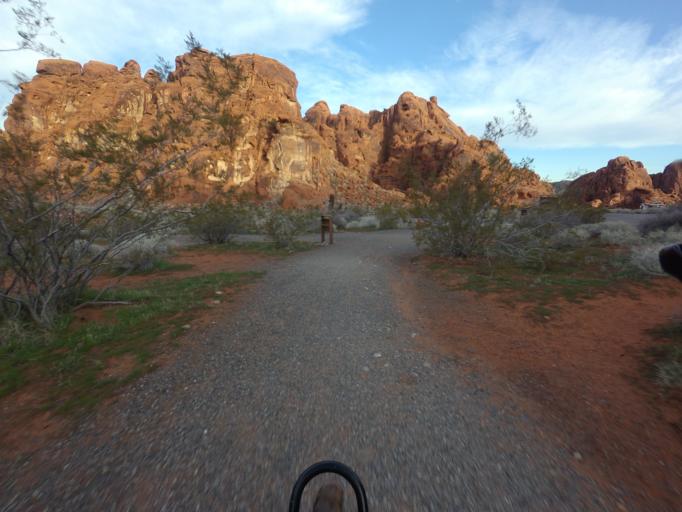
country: US
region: Nevada
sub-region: Clark County
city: Moapa Valley
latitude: 36.4158
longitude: -114.5536
